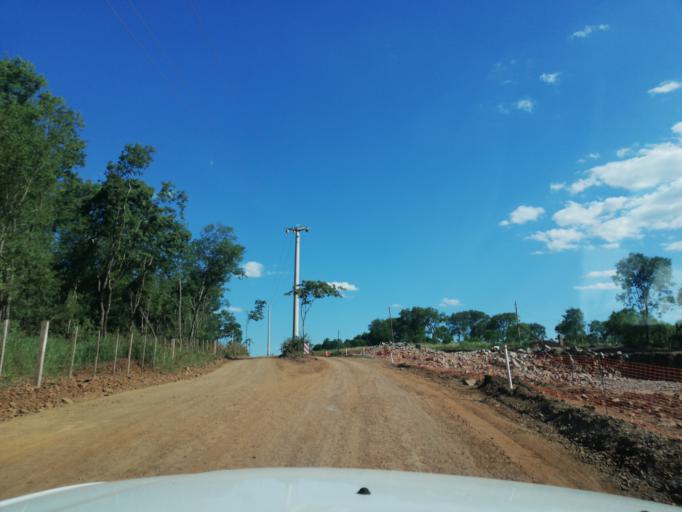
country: AR
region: Misiones
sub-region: Departamento de Candelaria
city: Candelaria
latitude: -27.5445
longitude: -55.7135
